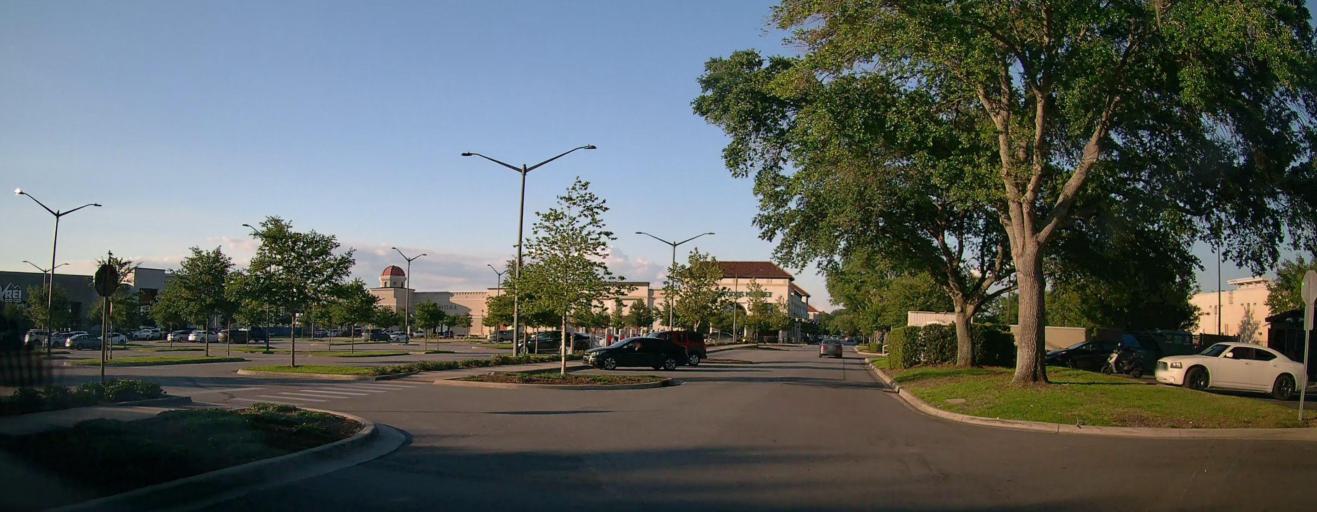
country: US
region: Florida
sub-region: Alachua County
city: Gainesville
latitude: 29.6242
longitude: -82.3770
